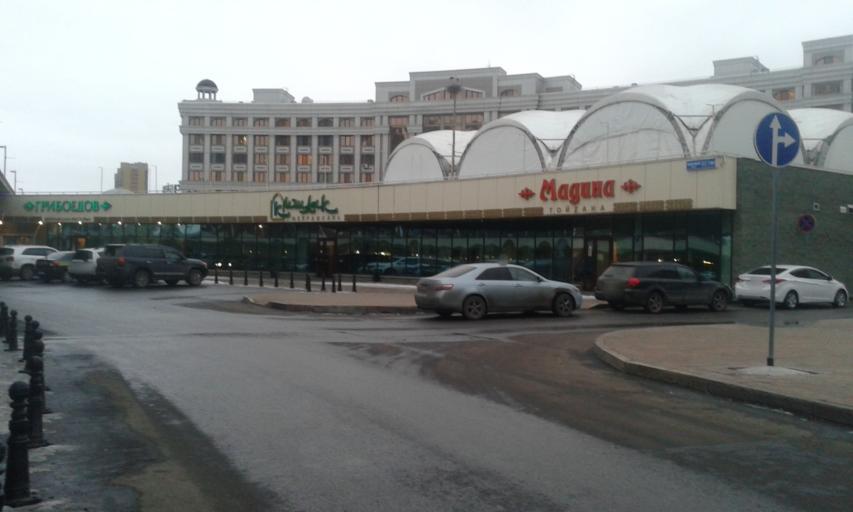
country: KZ
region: Astana Qalasy
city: Astana
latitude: 51.1309
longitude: 71.4138
